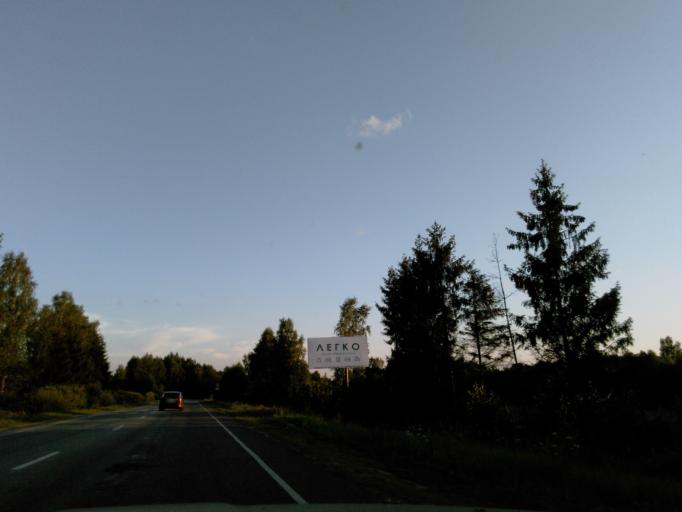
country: RU
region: Tverskaya
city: Konakovo
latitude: 56.6585
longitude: 36.7154
